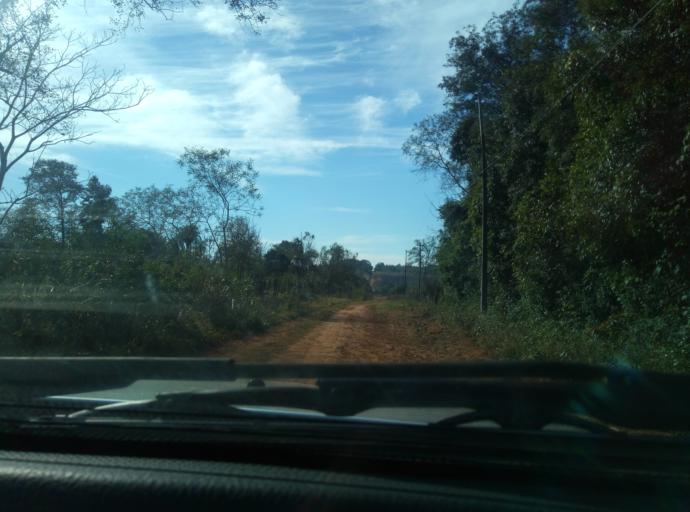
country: PY
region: Caaguazu
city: Carayao
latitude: -25.1708
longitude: -56.2933
